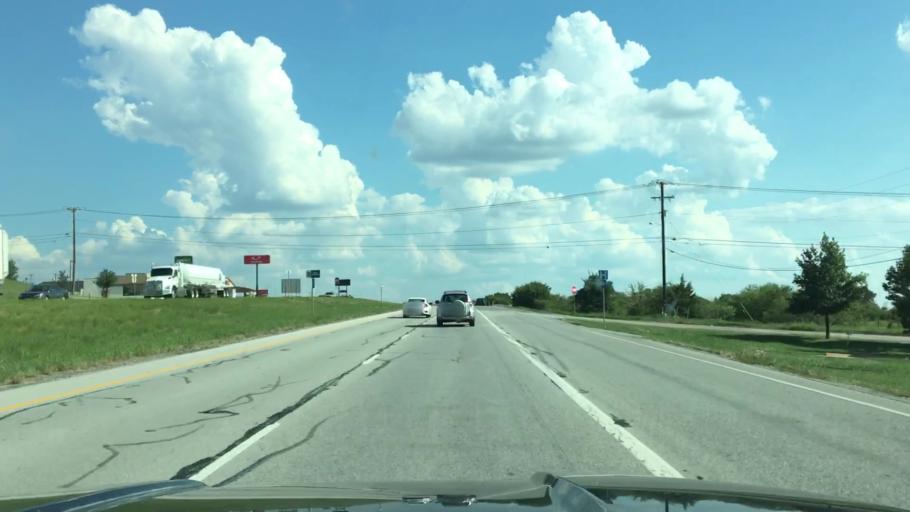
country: US
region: Texas
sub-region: Wise County
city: Decatur
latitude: 33.2222
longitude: -97.5904
